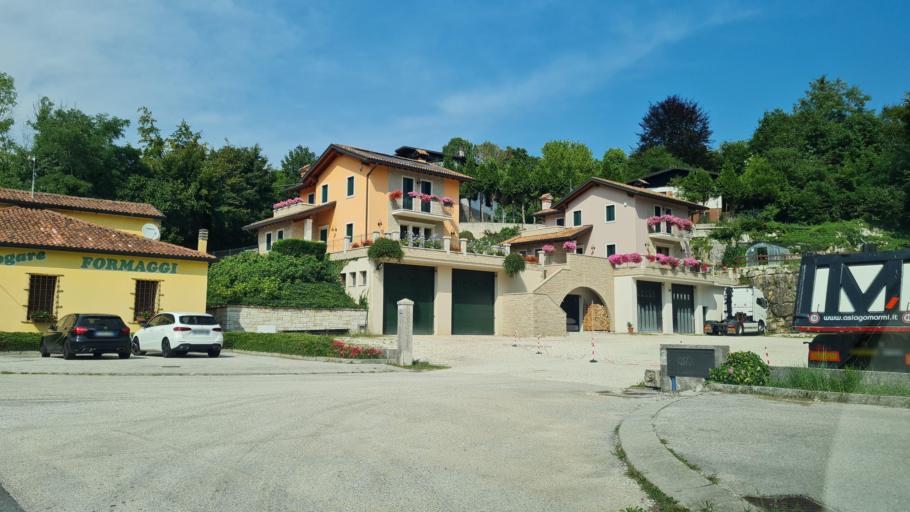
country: IT
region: Veneto
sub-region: Provincia di Vicenza
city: Conco
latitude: 45.7938
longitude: 11.6315
